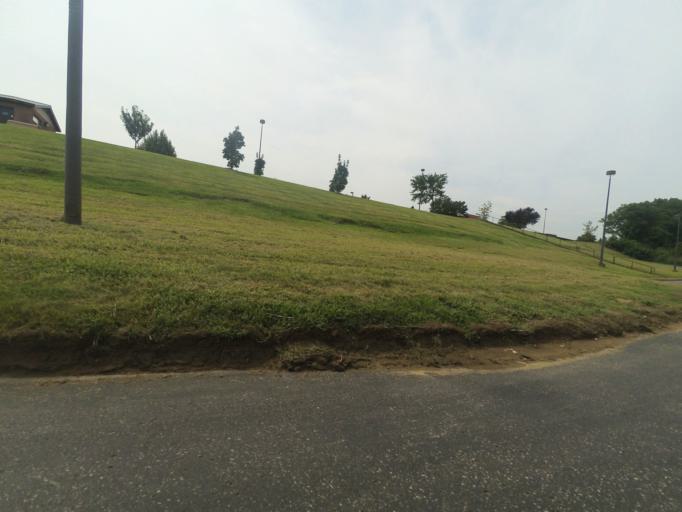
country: US
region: West Virginia
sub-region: Cabell County
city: Huntington
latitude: 38.4239
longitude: -82.4456
